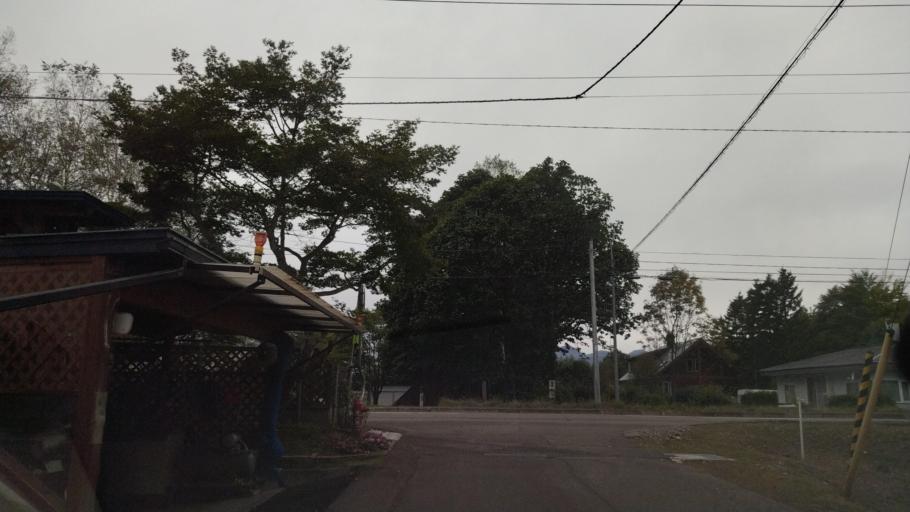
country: JP
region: Hokkaido
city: Otofuke
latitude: 43.2282
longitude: 143.2803
